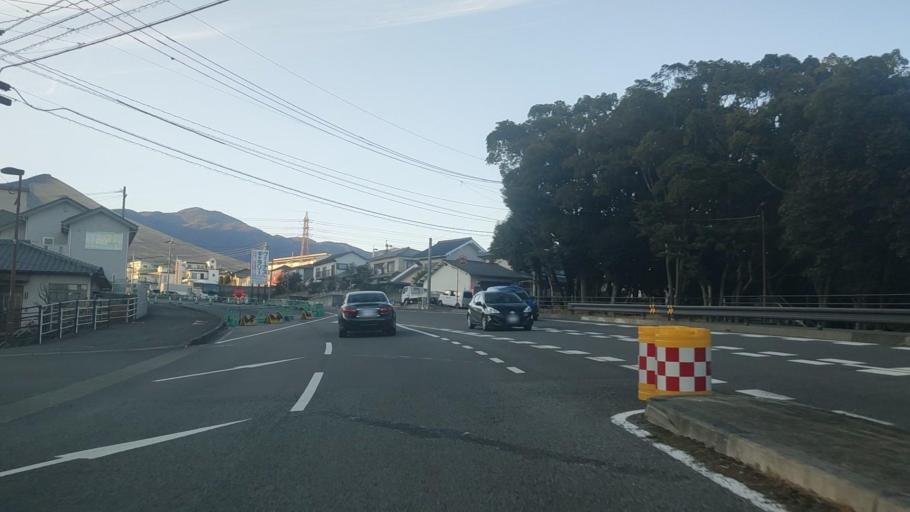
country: JP
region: Oita
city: Beppu
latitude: 33.2887
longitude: 131.4724
